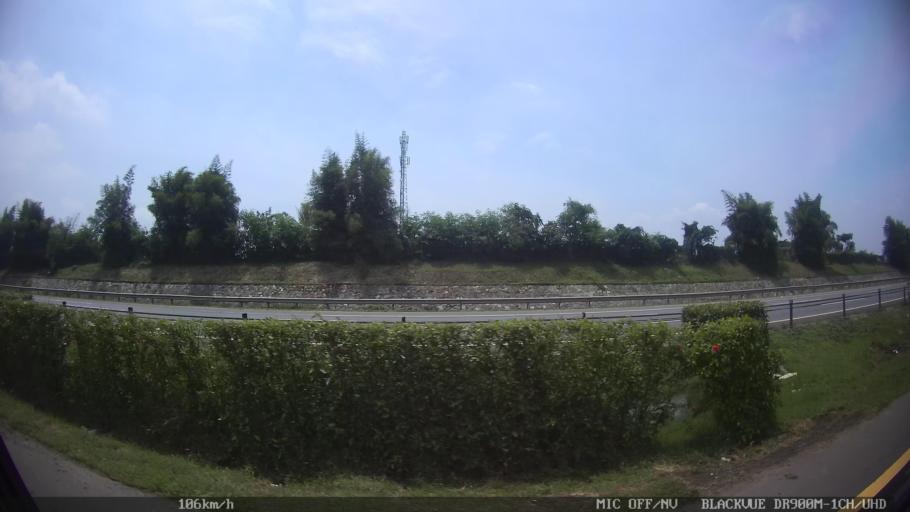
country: ID
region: West Java
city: Kresek
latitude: -6.1773
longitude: 106.3606
